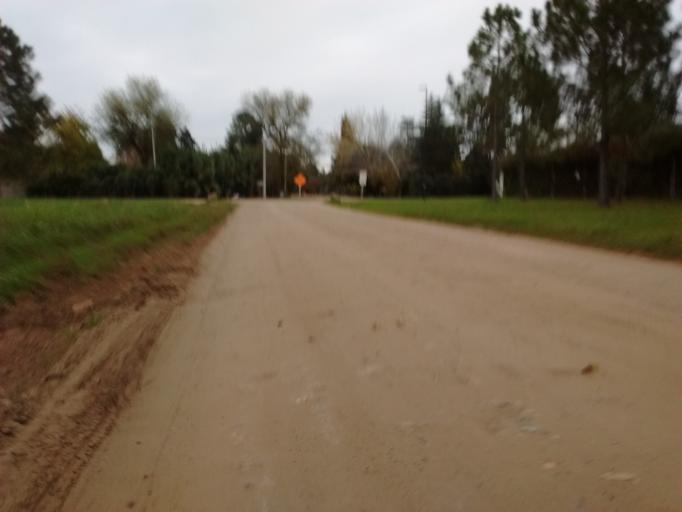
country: AR
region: Santa Fe
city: Funes
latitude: -32.9246
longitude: -60.8278
